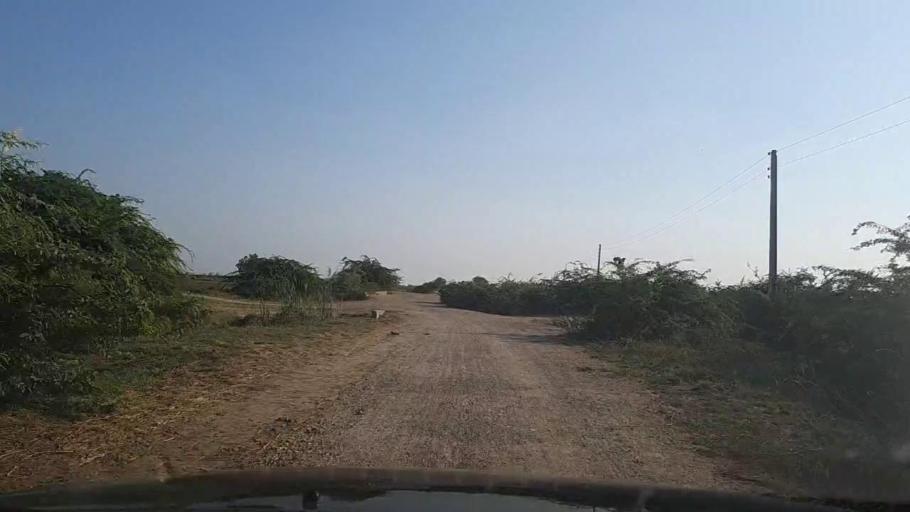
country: PK
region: Sindh
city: Gharo
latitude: 24.7087
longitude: 67.7040
